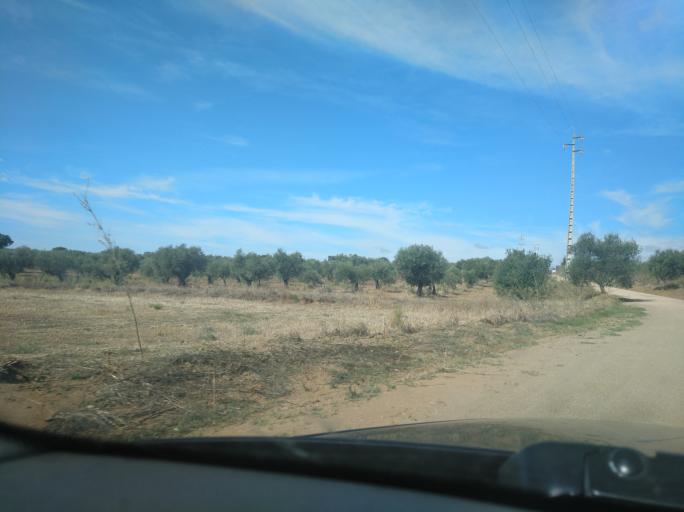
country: PT
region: Portalegre
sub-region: Campo Maior
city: Campo Maior
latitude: 39.0482
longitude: -7.0506
